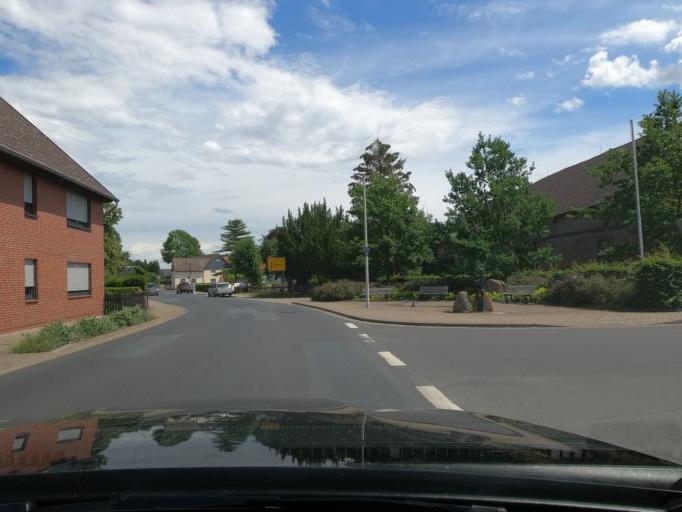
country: DE
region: Lower Saxony
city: Lengede
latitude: 52.1875
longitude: 10.2892
